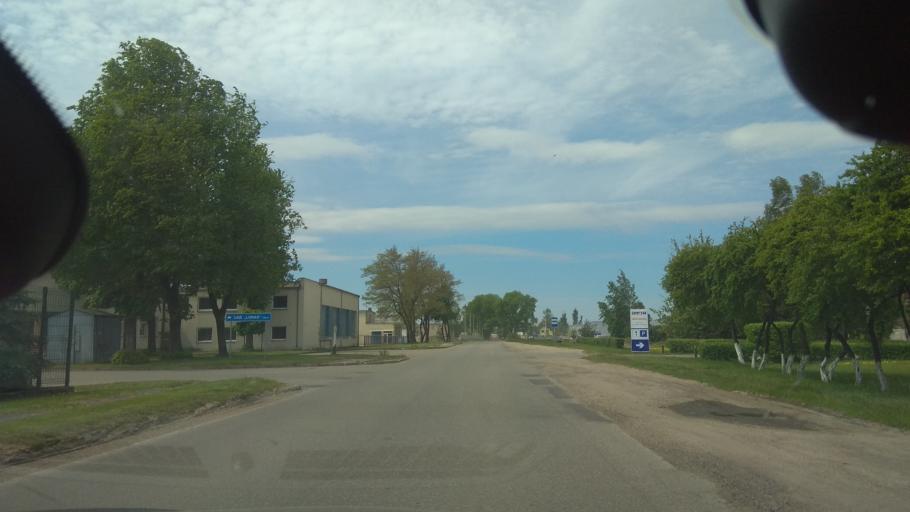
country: LT
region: Kauno apskritis
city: Jonava
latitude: 55.0901
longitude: 24.2871
